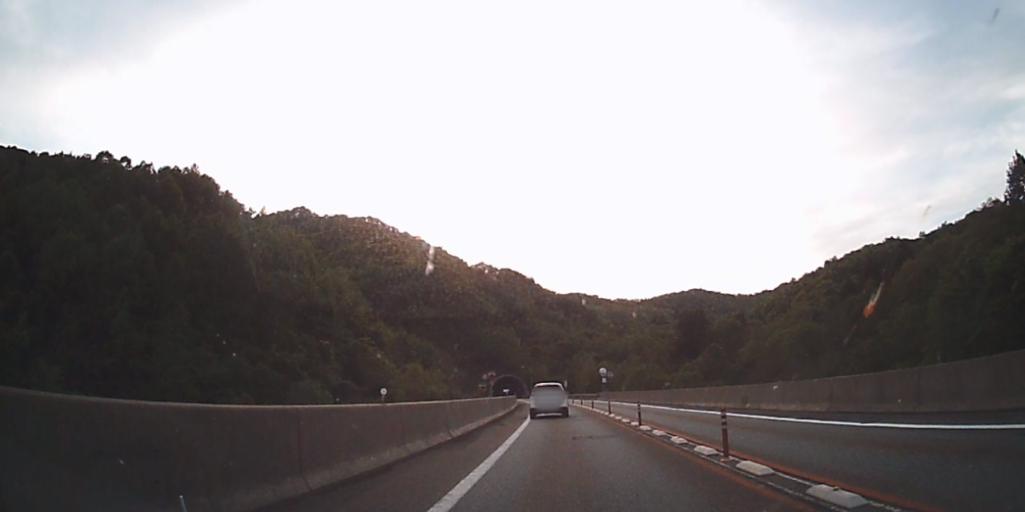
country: JP
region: Hokkaido
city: Date
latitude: 42.5726
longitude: 140.7471
